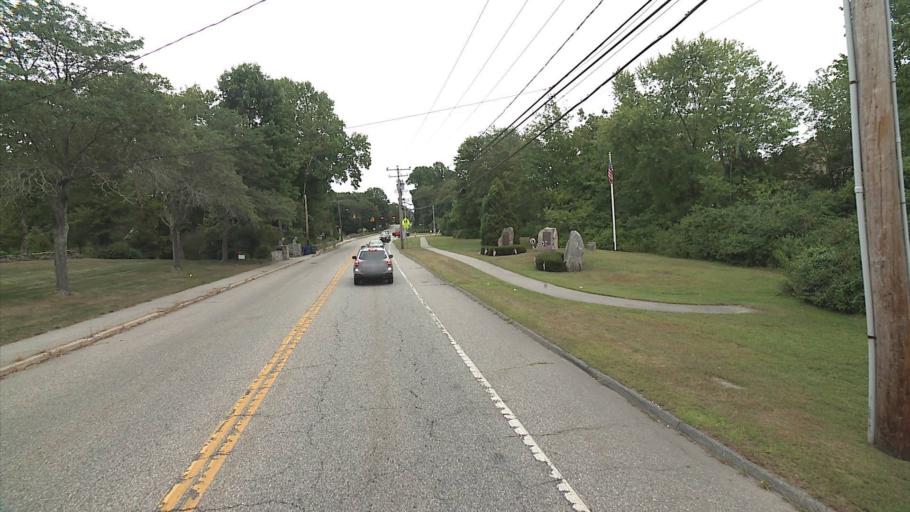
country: US
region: Connecticut
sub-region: New London County
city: Central Waterford
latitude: 41.3405
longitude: -72.1399
